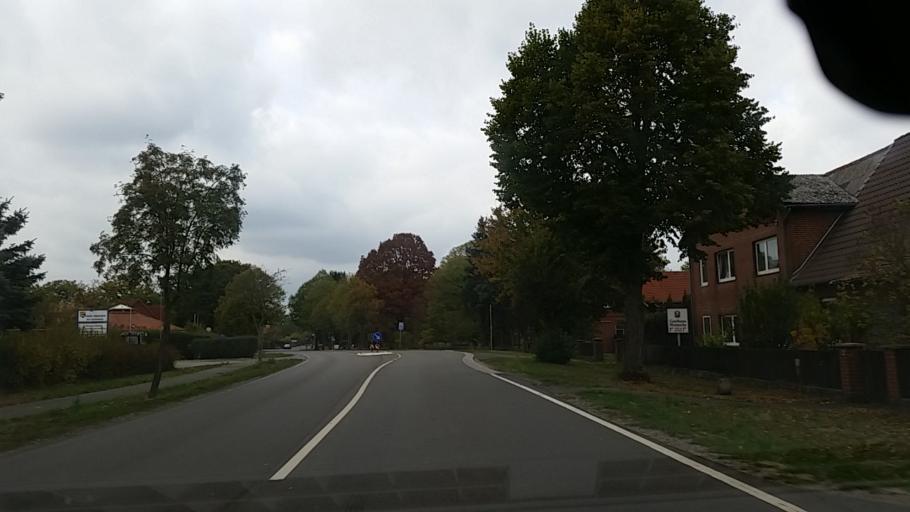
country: DE
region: Lower Saxony
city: Gross Oesingen
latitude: 52.6445
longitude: 10.4649
